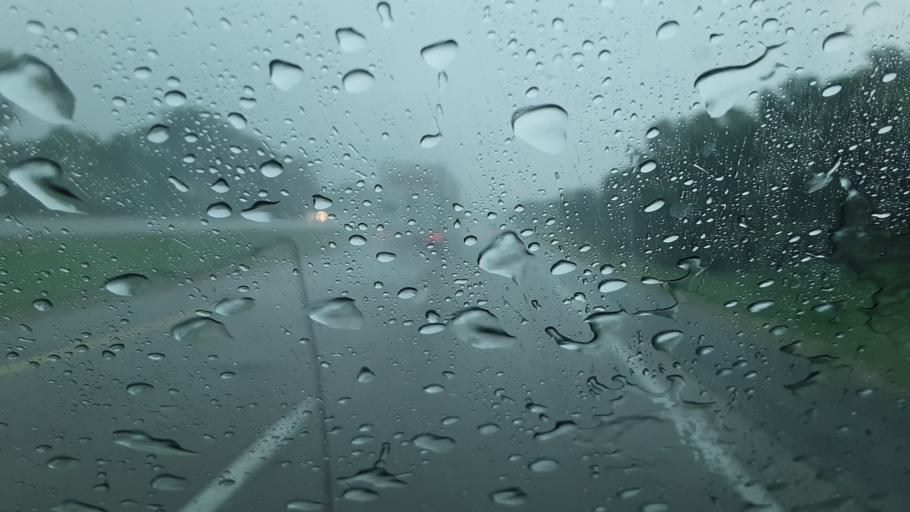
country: US
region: Iowa
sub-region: Pottawattamie County
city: Council Bluffs
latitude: 41.2498
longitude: -95.8118
